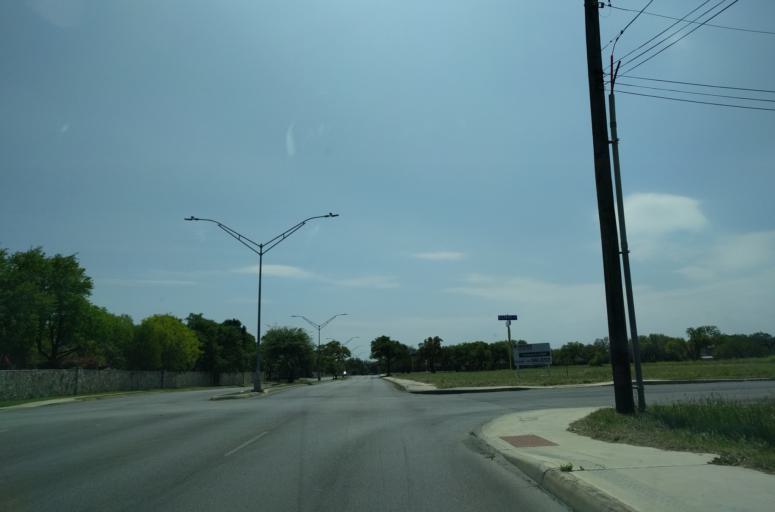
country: US
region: Texas
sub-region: Bexar County
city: Shavano Park
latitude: 29.5732
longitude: -98.5857
